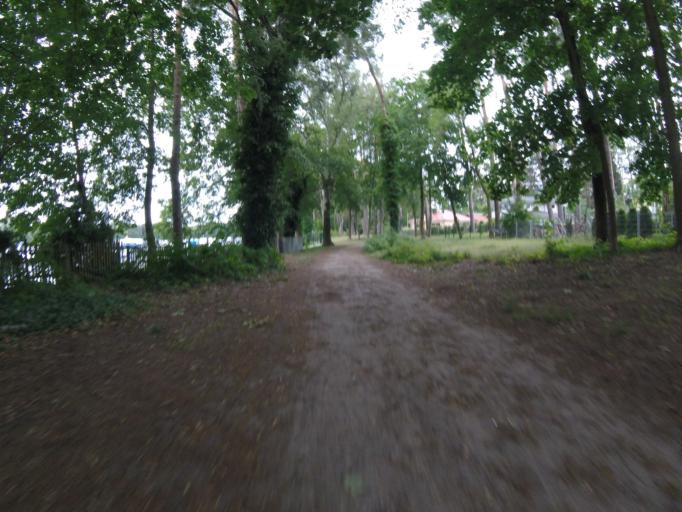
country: DE
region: Brandenburg
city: Bestensee
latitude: 52.2908
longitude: 13.7114
